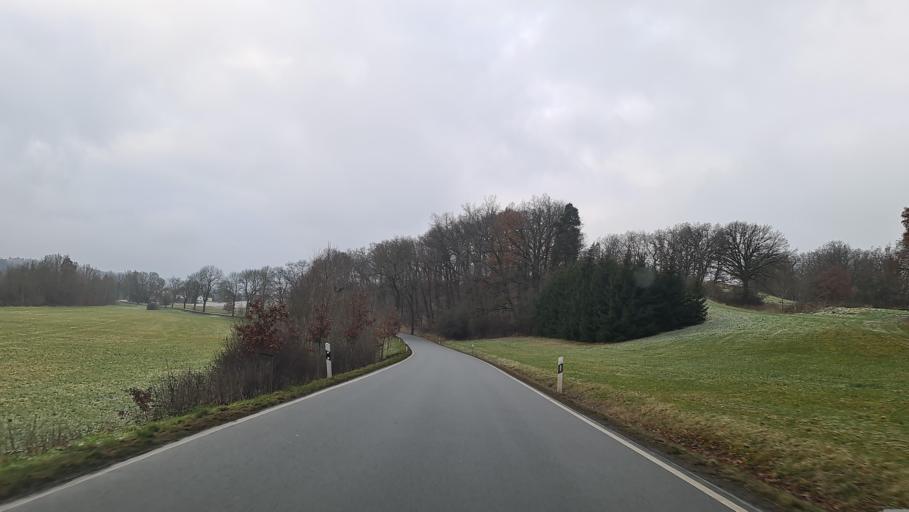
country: DE
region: Saxony
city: Weischlitz
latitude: 50.4698
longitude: 12.0713
